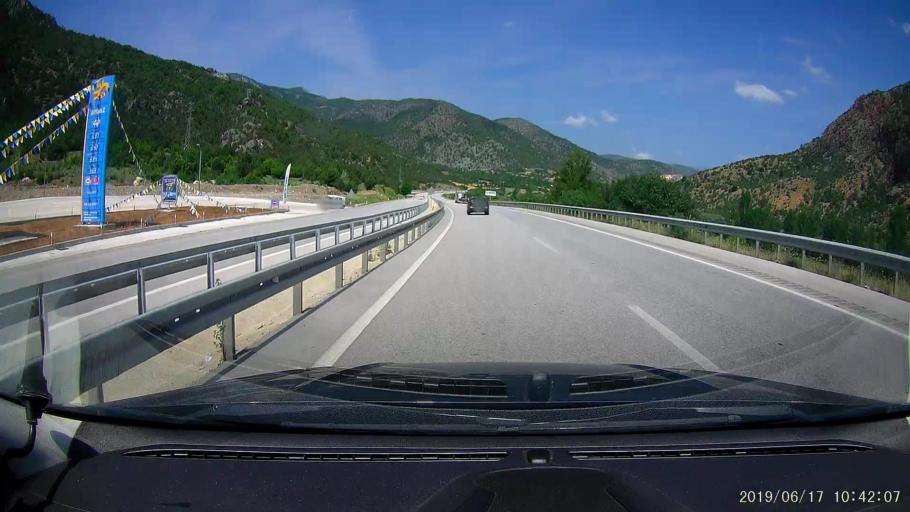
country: TR
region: Corum
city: Kargi
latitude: 41.0464
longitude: 34.5610
